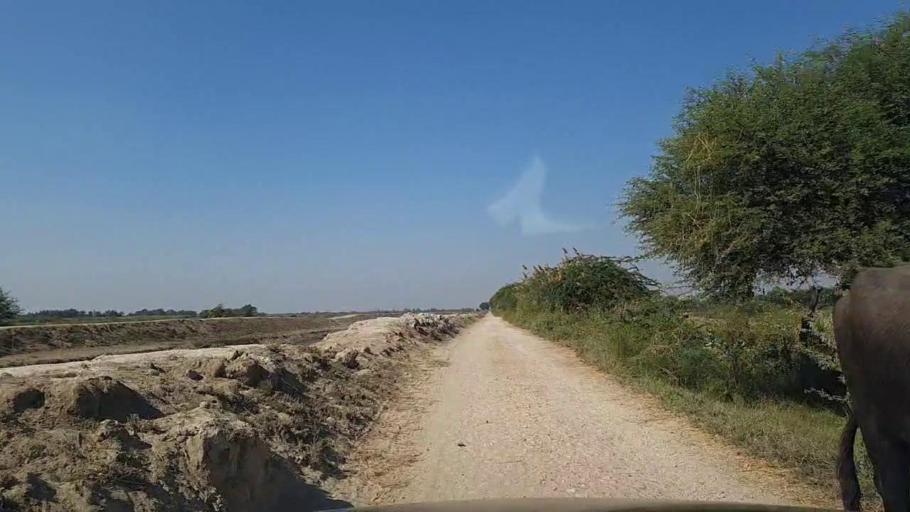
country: PK
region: Sindh
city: Mirpur Batoro
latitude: 24.7176
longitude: 68.2364
